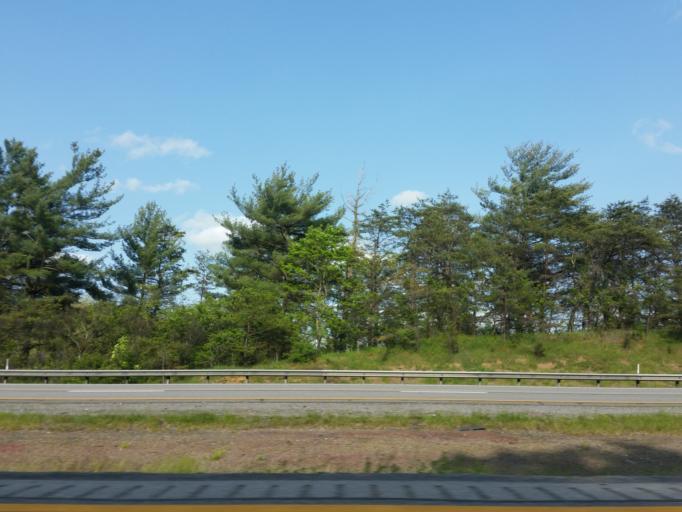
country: US
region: West Virginia
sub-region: Mercer County
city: Athens
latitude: 37.4409
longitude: -81.0647
